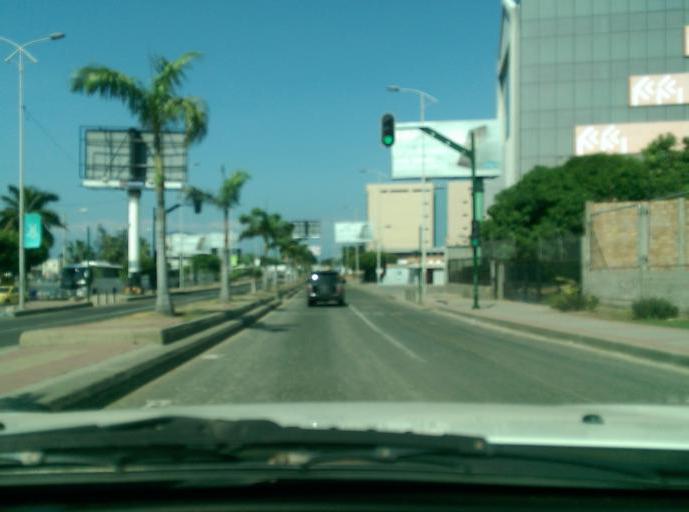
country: EC
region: Manabi
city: Manta
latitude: -0.9417
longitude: -80.7311
